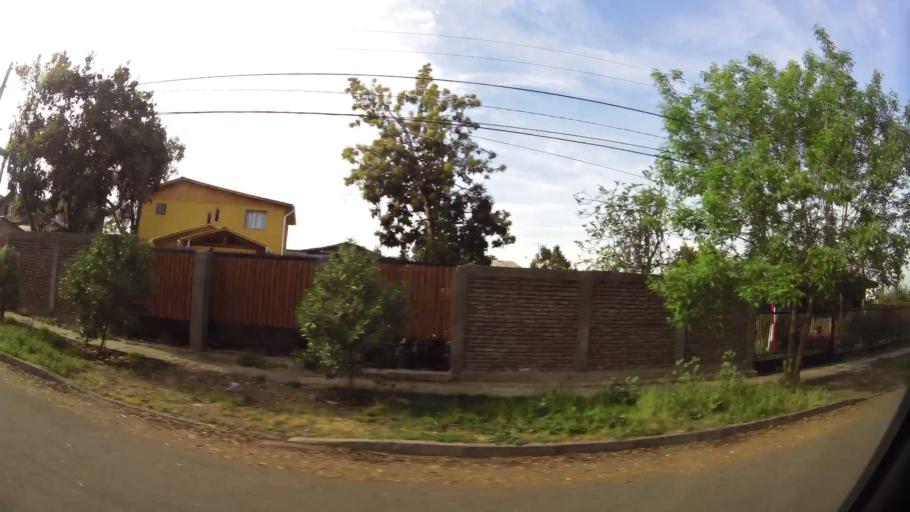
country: CL
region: Santiago Metropolitan
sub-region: Provincia de Talagante
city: Talagante
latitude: -33.6654
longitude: -70.9360
